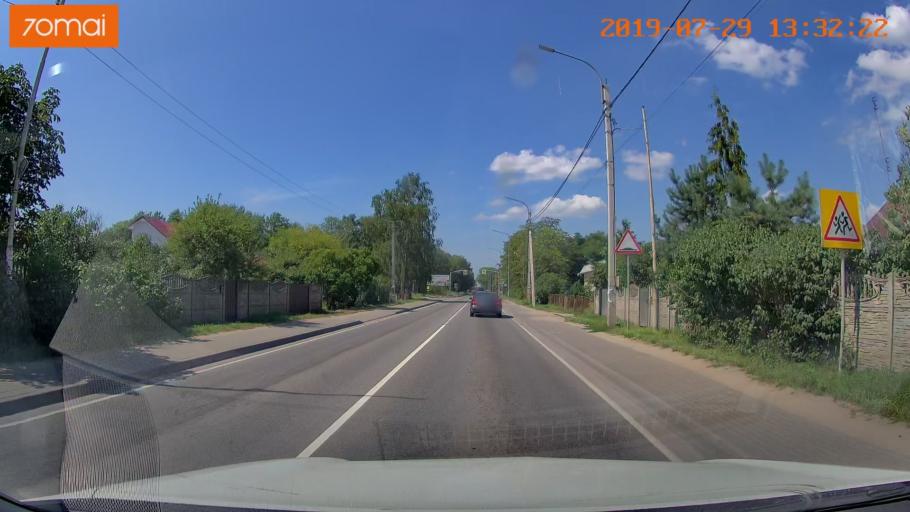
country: RU
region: Kaliningrad
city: Vzmorye
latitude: 54.6977
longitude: 20.2361
